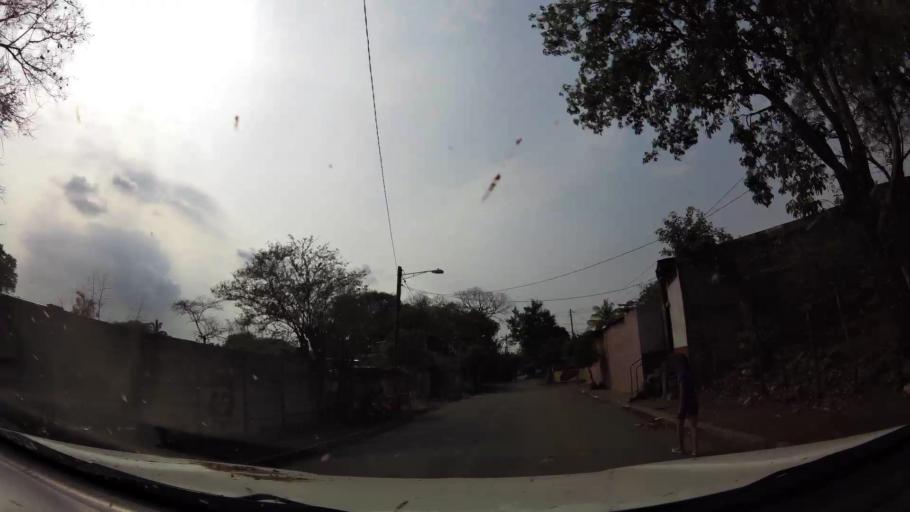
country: NI
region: Masaya
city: Masaya
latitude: 11.9700
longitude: -86.0971
